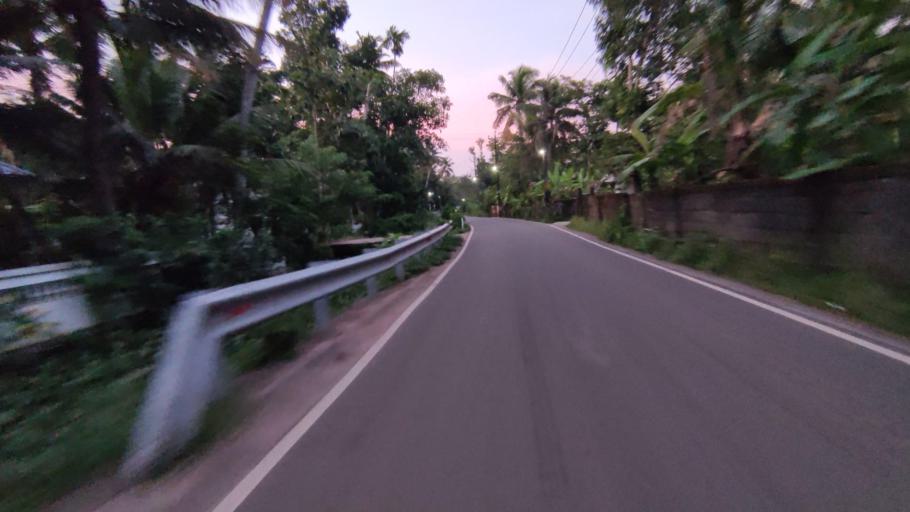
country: IN
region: Kerala
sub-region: Kottayam
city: Kottayam
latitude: 9.5838
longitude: 76.4361
